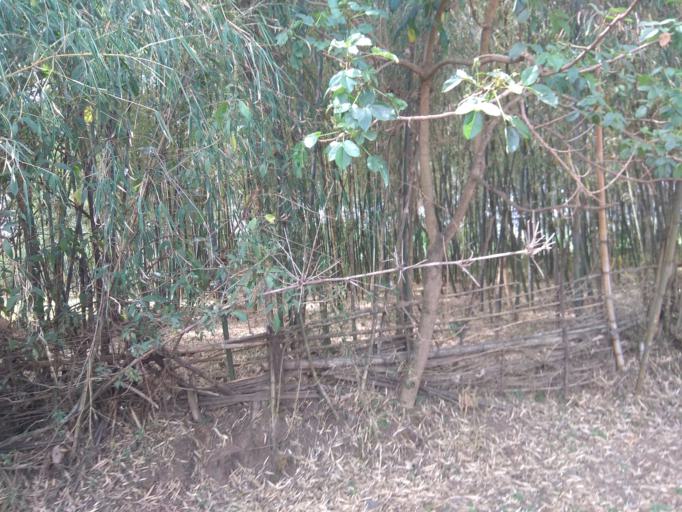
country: ET
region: Oromiya
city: Guder
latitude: 8.8097
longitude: 37.6415
